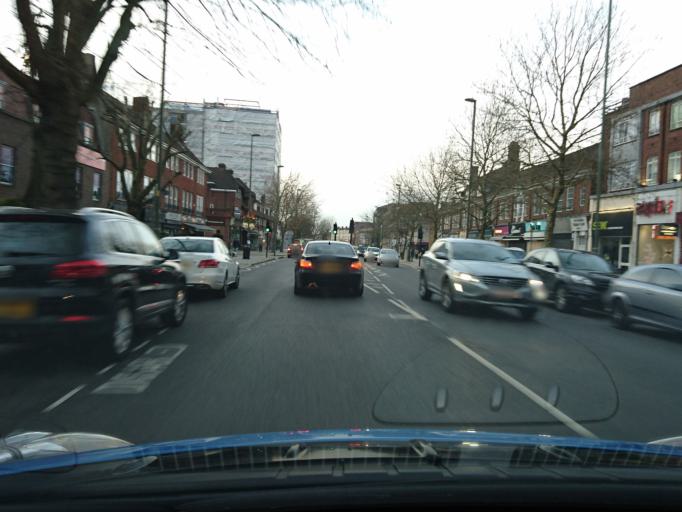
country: GB
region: England
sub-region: Greater London
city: Barnet
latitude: 51.6320
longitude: -0.1755
